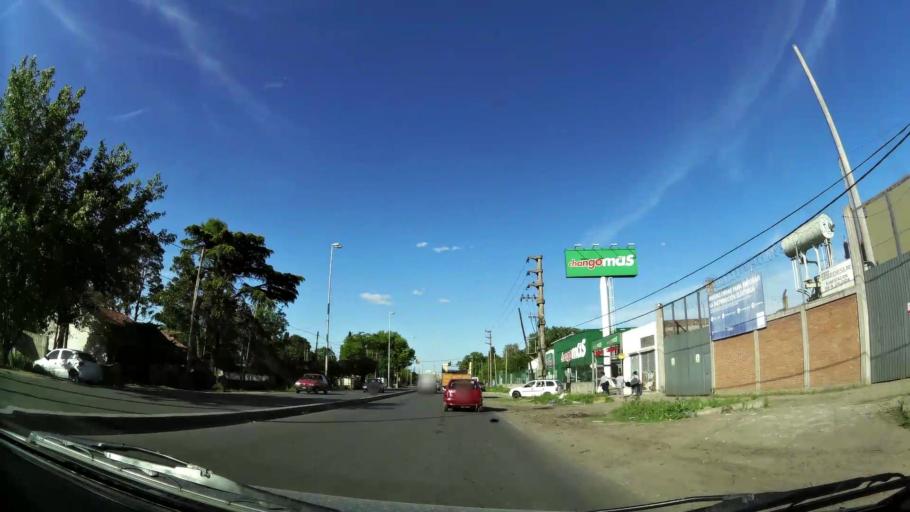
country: AR
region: Buenos Aires
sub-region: Partido de Almirante Brown
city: Adrogue
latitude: -34.8094
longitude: -58.3445
